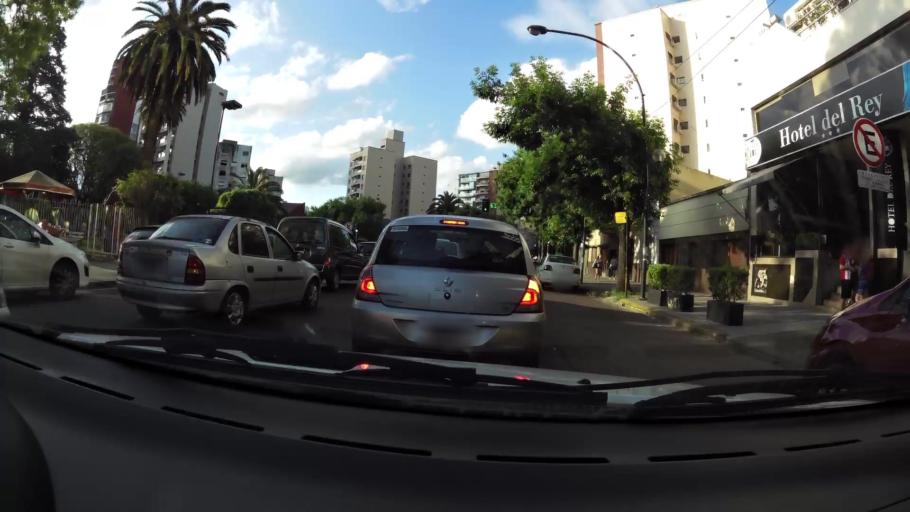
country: AR
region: Buenos Aires
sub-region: Partido de La Plata
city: La Plata
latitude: -34.9162
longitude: -57.9609
